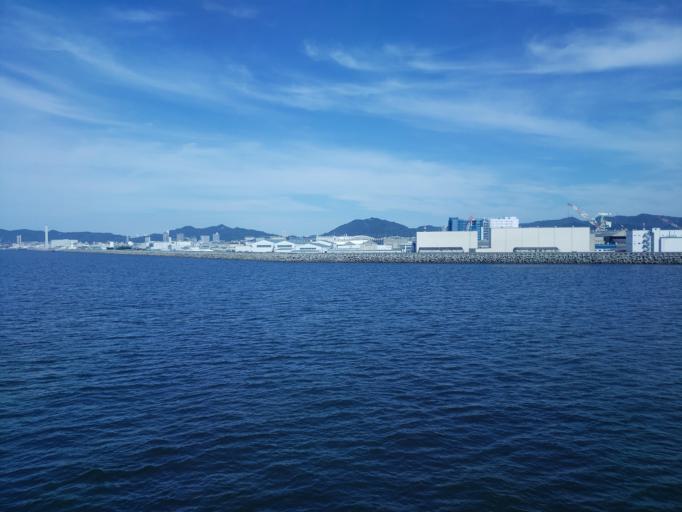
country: JP
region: Hyogo
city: Kobe
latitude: 34.6480
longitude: 135.1879
